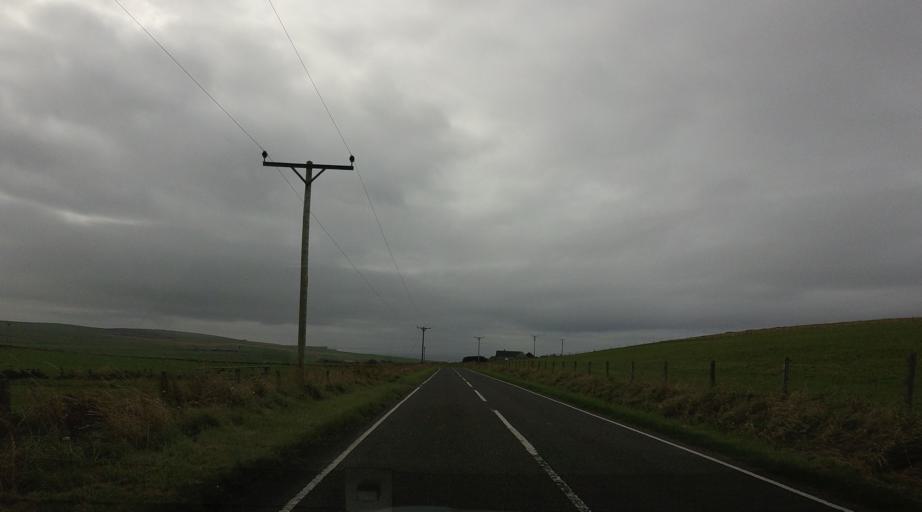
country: GB
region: Scotland
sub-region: Orkney Islands
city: Orkney
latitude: 58.7971
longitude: -2.9657
